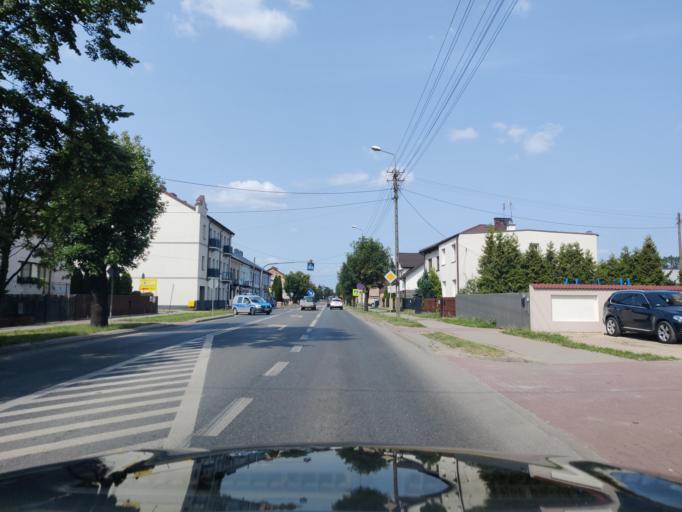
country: PL
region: Masovian Voivodeship
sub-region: Powiat pultuski
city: Pultusk
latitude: 52.7090
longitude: 21.0837
